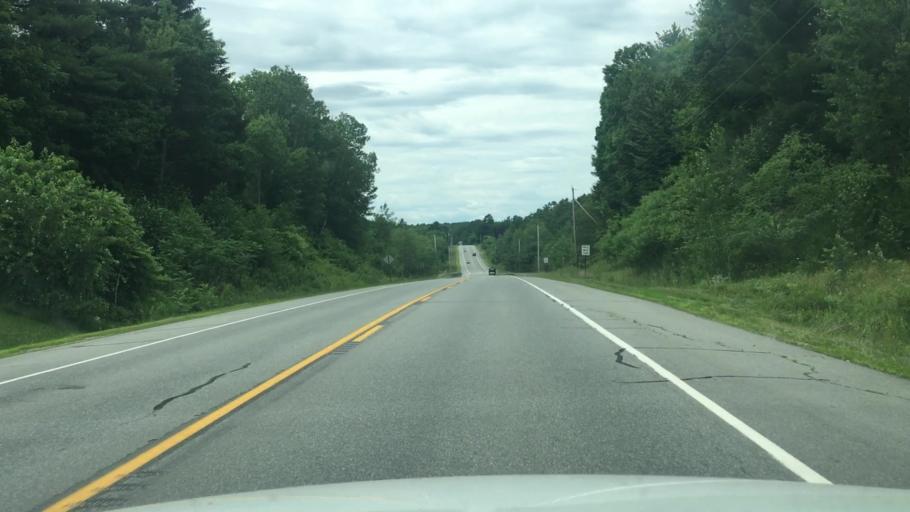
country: US
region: Maine
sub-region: Kennebec County
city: Windsor
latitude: 44.3858
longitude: -69.6024
